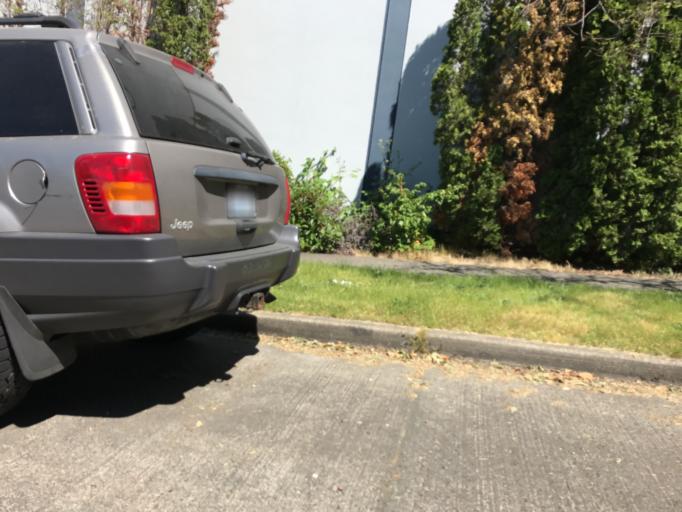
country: US
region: Washington
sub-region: King County
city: Seattle
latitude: 47.5845
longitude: -122.2984
